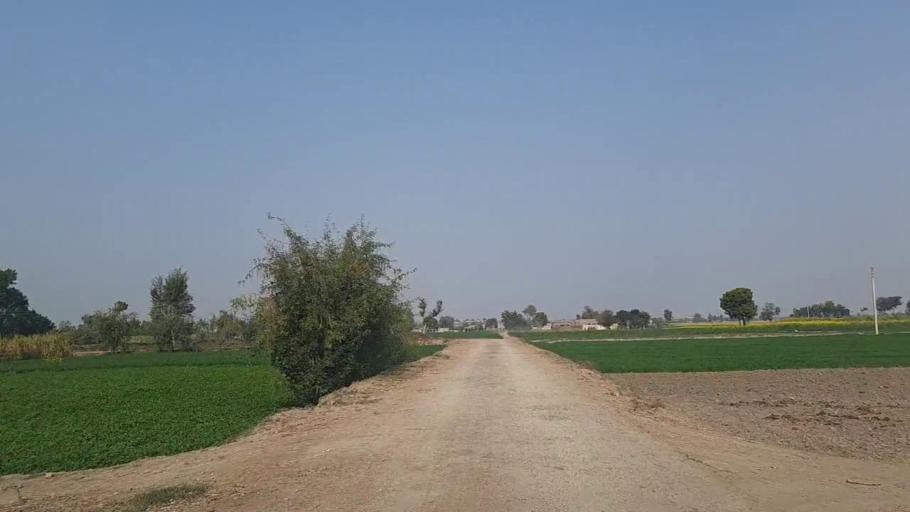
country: PK
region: Sindh
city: Daur
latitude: 26.4771
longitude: 68.4824
